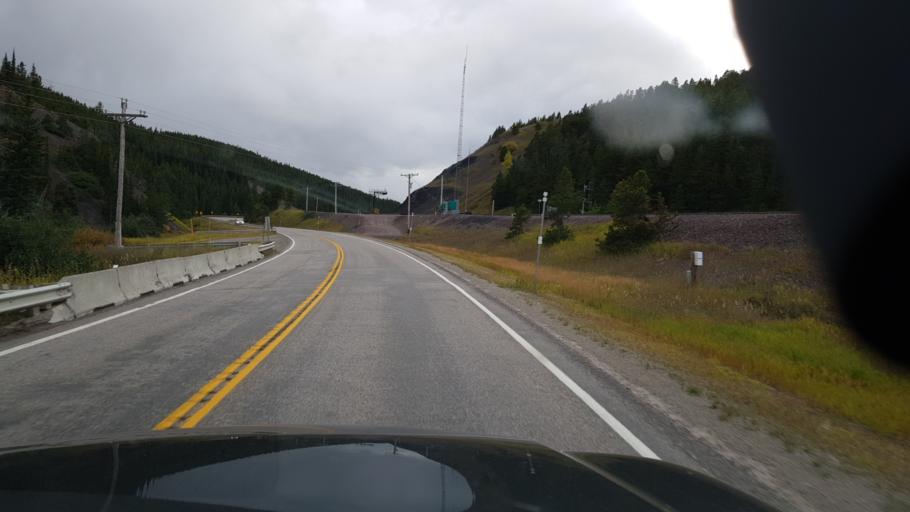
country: US
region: Montana
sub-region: Glacier County
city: South Browning
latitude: 48.3308
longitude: -113.3382
